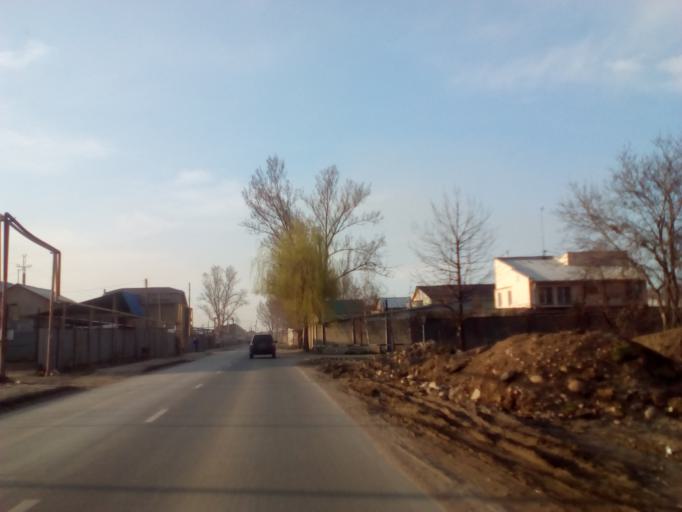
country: KZ
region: Almaty Oblysy
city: Burunday
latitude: 43.2427
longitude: 76.7879
